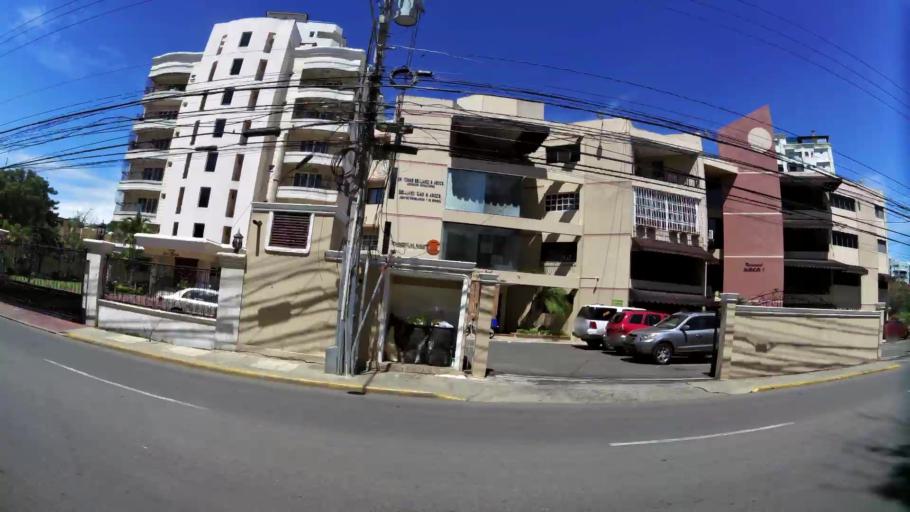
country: DO
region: Santiago
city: Santiago de los Caballeros
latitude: 19.4536
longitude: -70.6891
